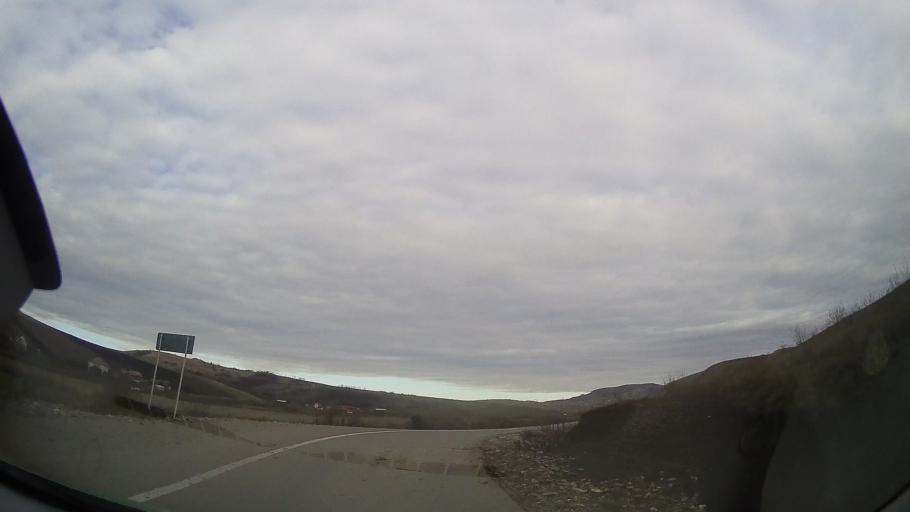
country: RO
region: Bistrita-Nasaud
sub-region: Comuna Silvasu de Campie
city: Silvasu de Campie
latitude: 46.7902
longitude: 24.2877
